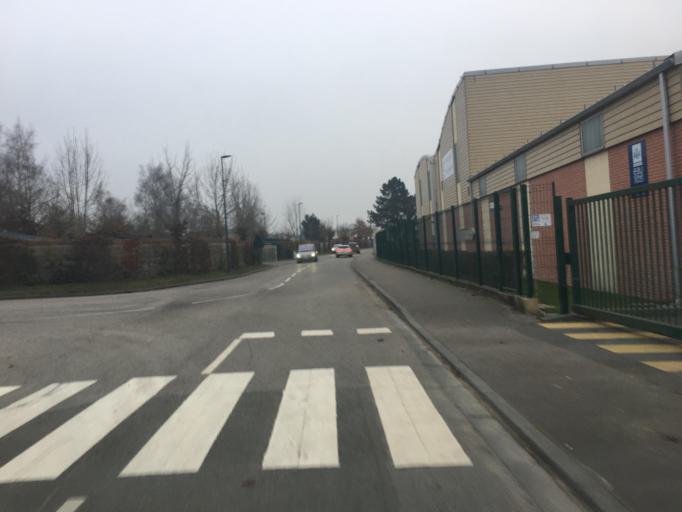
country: FR
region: Haute-Normandie
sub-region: Departement de la Seine-Maritime
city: Neufchatel-en-Bray
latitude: 49.7363
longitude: 1.4314
